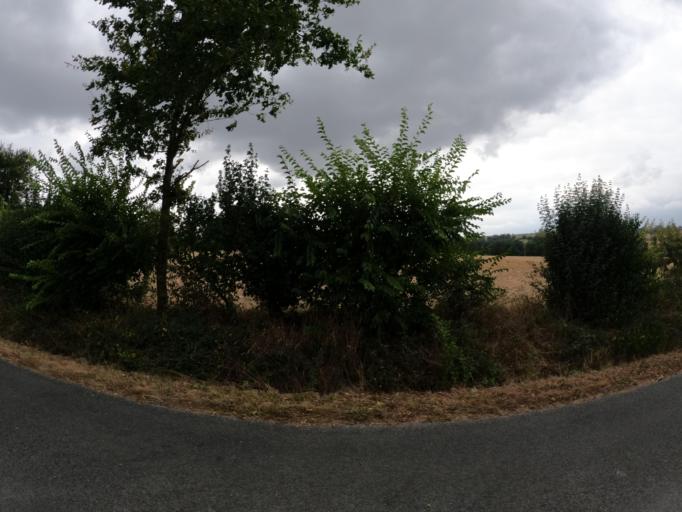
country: FR
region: Pays de la Loire
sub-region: Departement de Maine-et-Loire
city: Le Longeron
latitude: 46.9991
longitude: -1.0714
